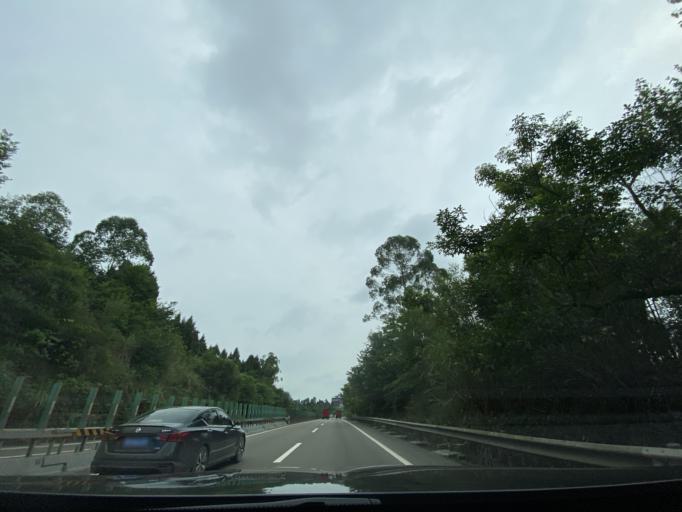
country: CN
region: Sichuan
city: Neijiang
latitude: 29.6509
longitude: 104.9845
